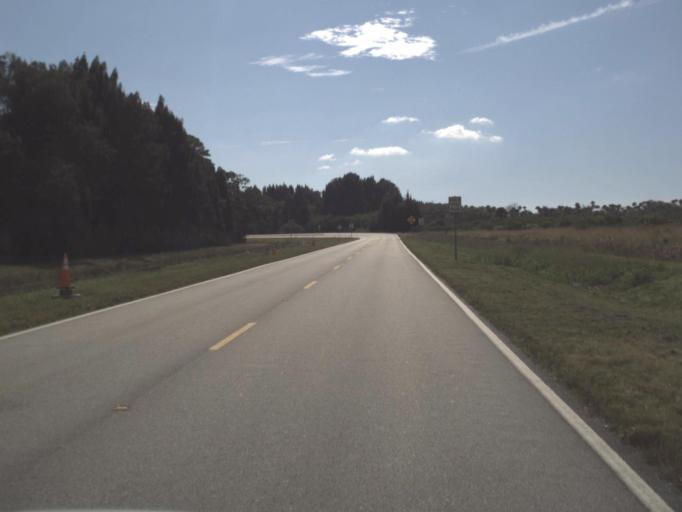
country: US
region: Florida
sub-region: Brevard County
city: Merritt Island
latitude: 28.5048
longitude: -80.6756
